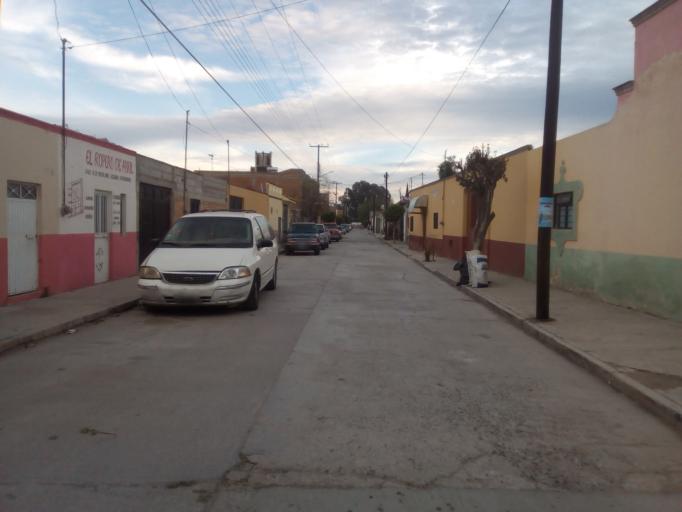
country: MX
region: Guanajuato
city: San Jose Iturbide
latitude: 21.0067
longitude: -100.3883
